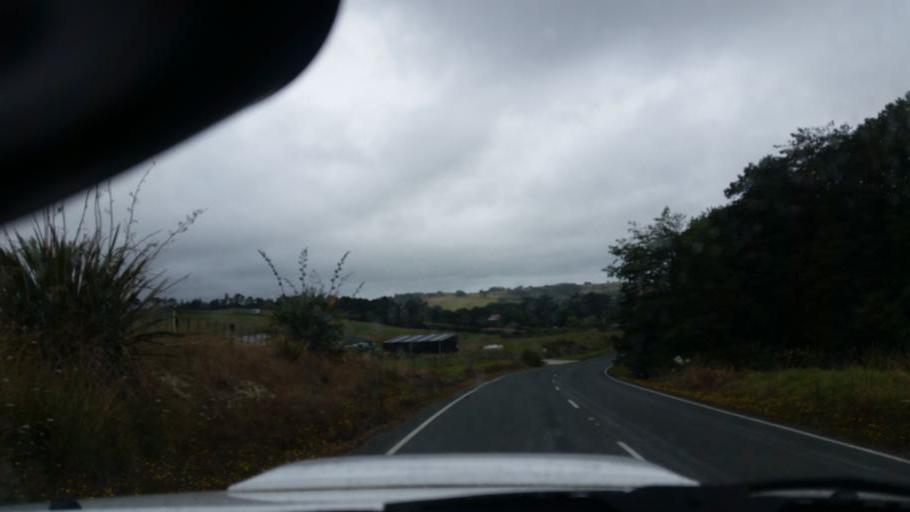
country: NZ
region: Auckland
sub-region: Auckland
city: Wellsford
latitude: -36.1419
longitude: 174.5003
